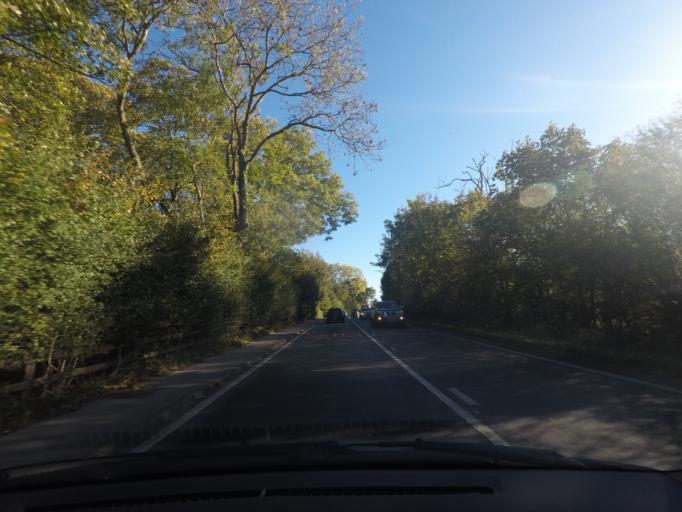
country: GB
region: England
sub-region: East Riding of Yorkshire
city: Wilberfoss
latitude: 53.9528
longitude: -0.9231
